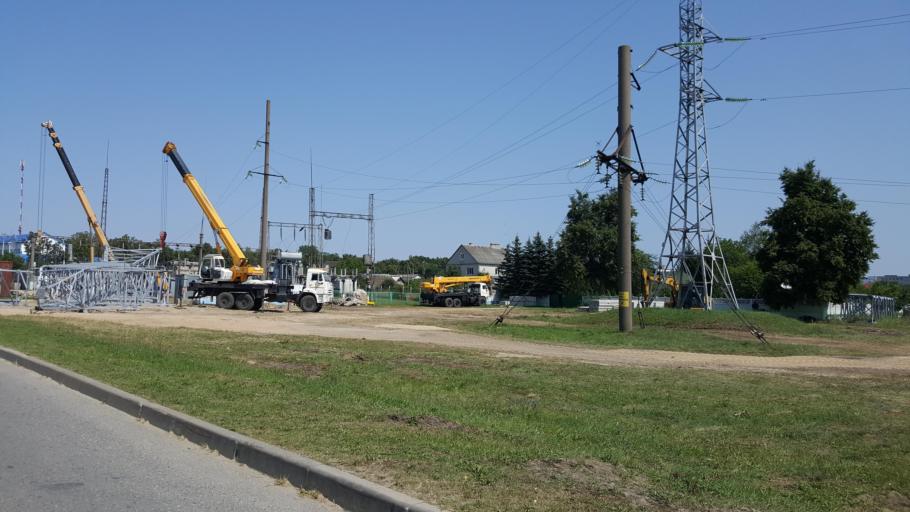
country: BY
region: Brest
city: Zhabinka
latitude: 52.1922
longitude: 24.0184
